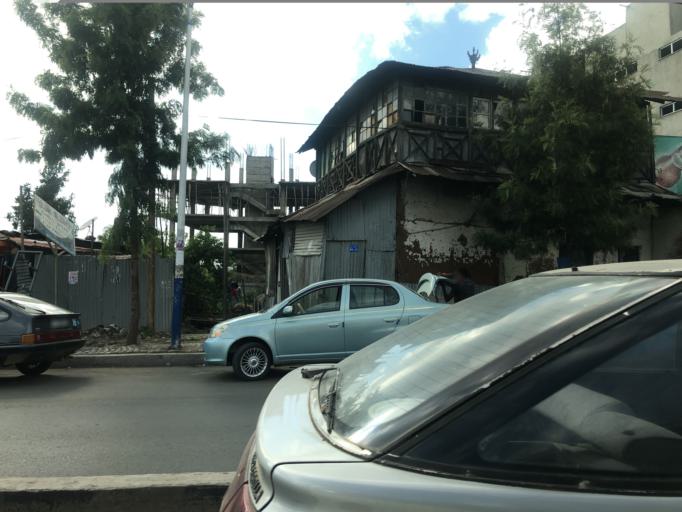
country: ET
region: Adis Abeba
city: Addis Ababa
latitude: 9.0194
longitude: 38.7825
